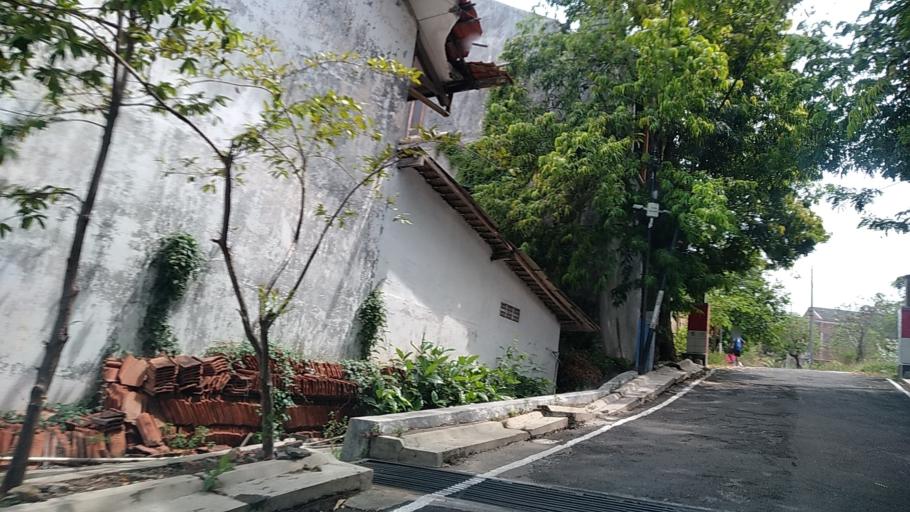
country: ID
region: Central Java
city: Semarang
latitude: -7.0411
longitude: 110.4425
